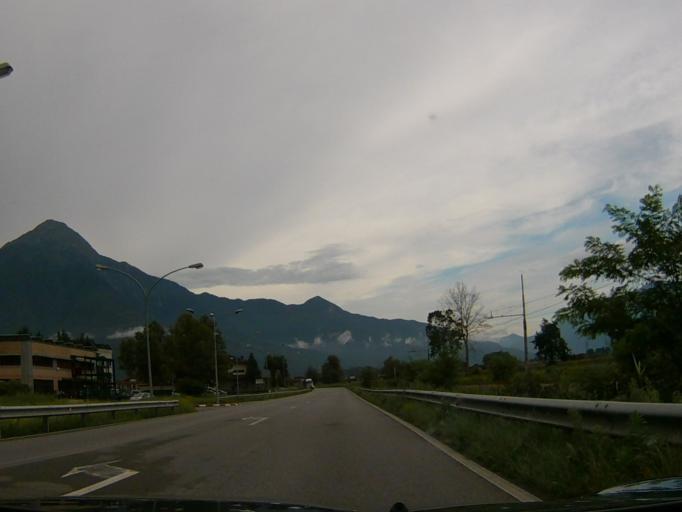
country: IT
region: Lombardy
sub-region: Provincia di Sondrio
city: Dubino
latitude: 46.1767
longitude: 9.4361
